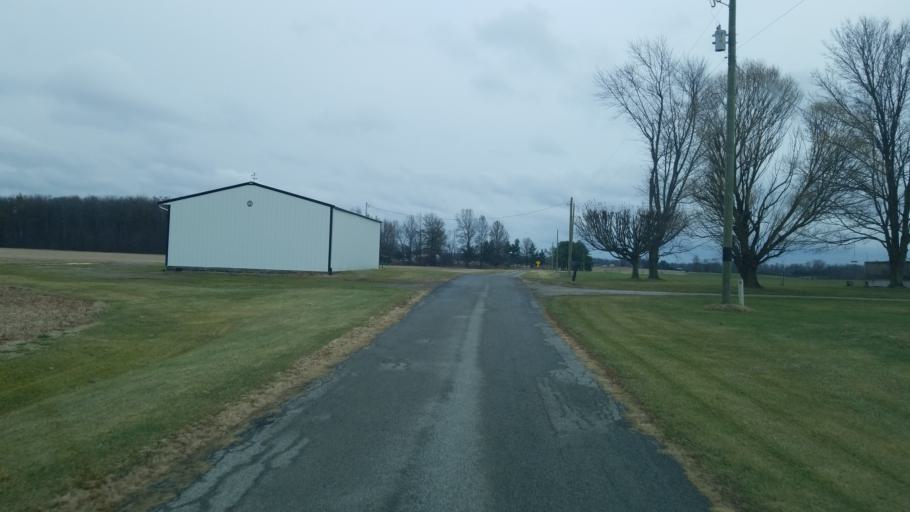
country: US
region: Ohio
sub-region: Union County
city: Marysville
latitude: 40.2959
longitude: -83.2849
